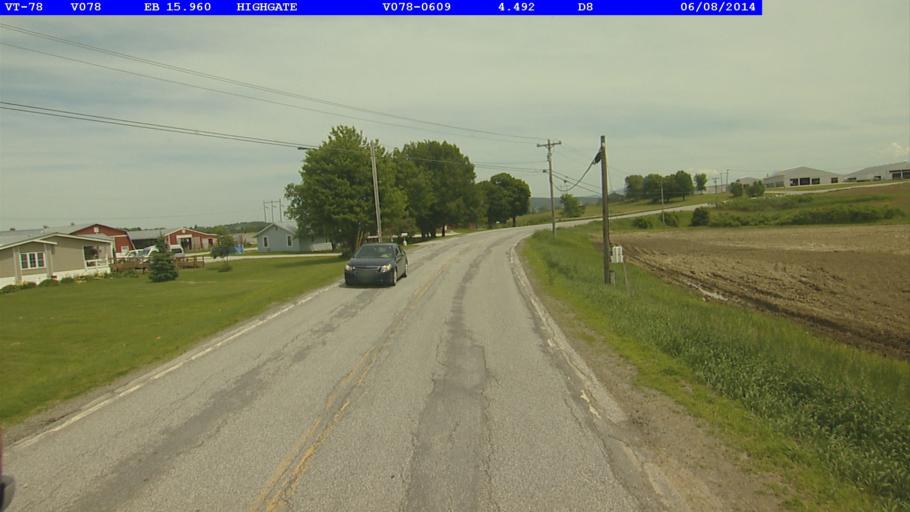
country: US
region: Vermont
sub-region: Franklin County
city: Swanton
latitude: 44.9462
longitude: -73.0185
